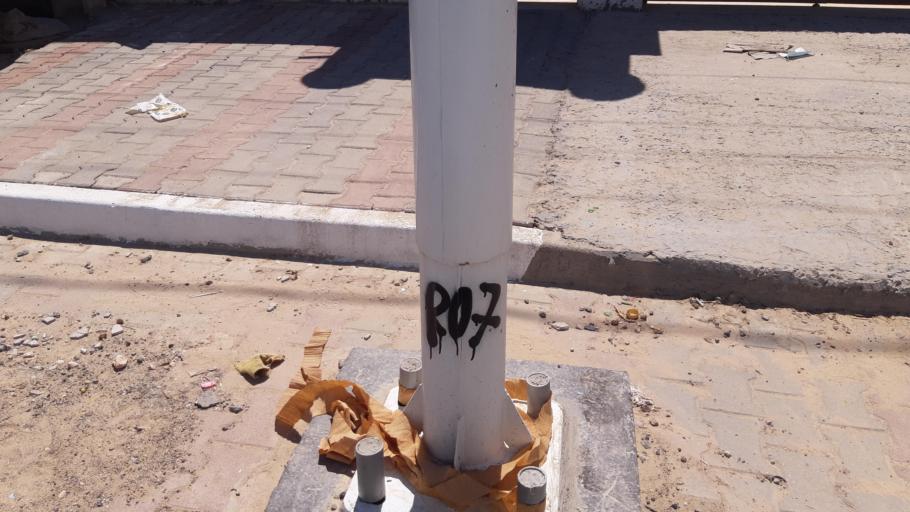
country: TN
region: Safaqis
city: Sfax
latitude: 34.7595
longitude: 10.7373
